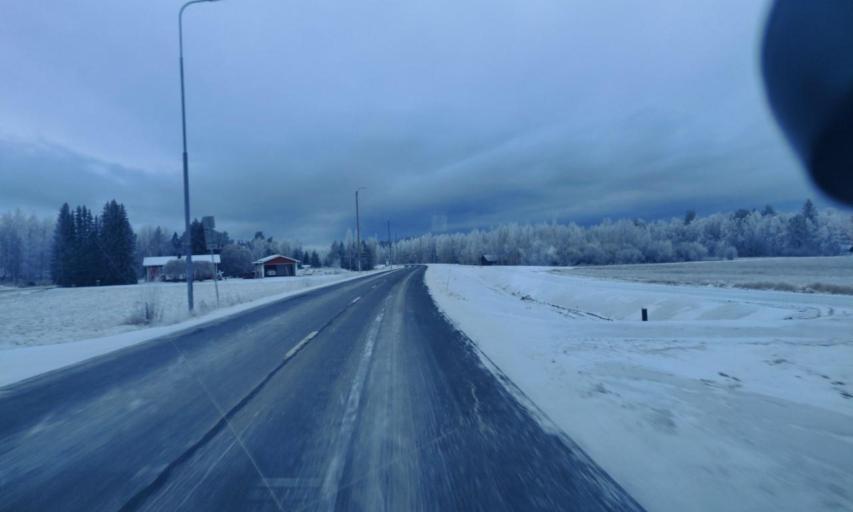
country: FI
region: Northern Ostrobothnia
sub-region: Oulu
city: Oulunsalo
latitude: 64.9806
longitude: 25.2732
